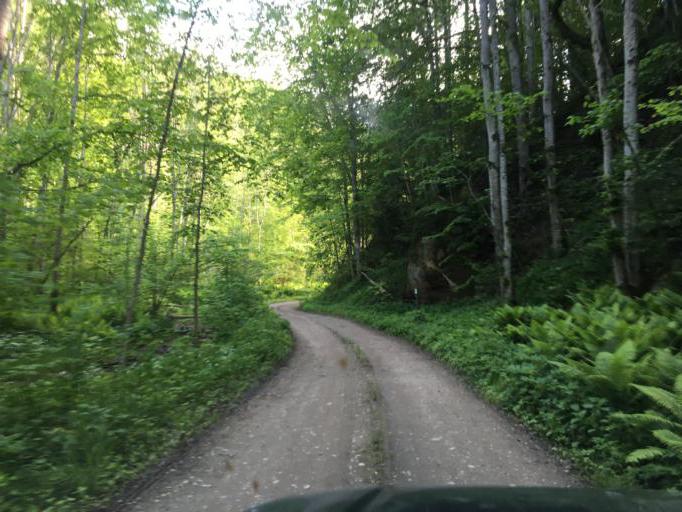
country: LV
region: Dundaga
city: Dundaga
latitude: 57.6261
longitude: 22.4218
